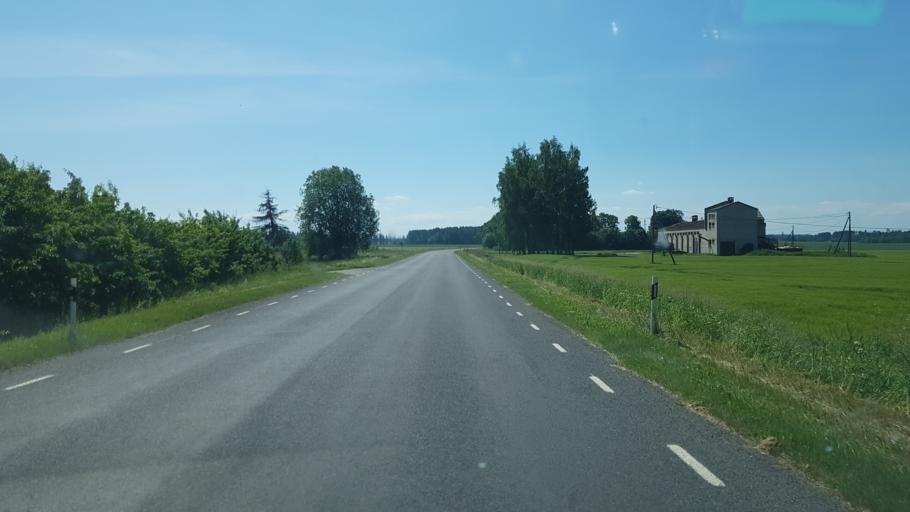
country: EE
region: Tartu
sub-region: UElenurme vald
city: Ulenurme
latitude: 58.3208
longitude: 26.8840
